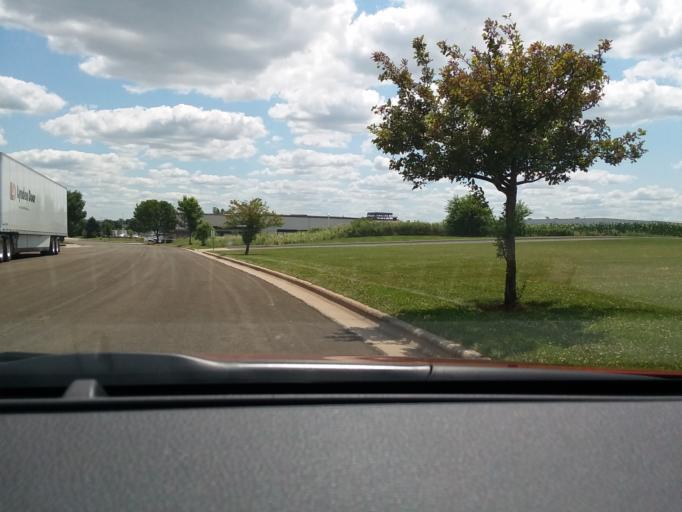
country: US
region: Wisconsin
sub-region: Dane County
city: Windsor
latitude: 43.2024
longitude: -89.3357
